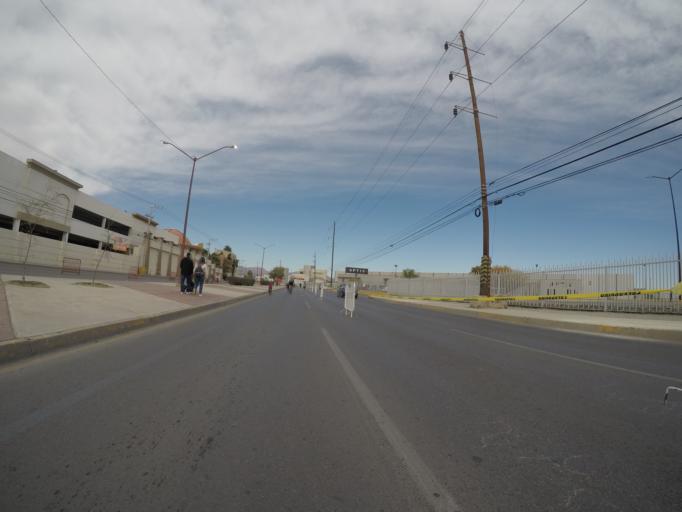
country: MX
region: Chihuahua
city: Ciudad Juarez
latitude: 31.7224
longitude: -106.3995
